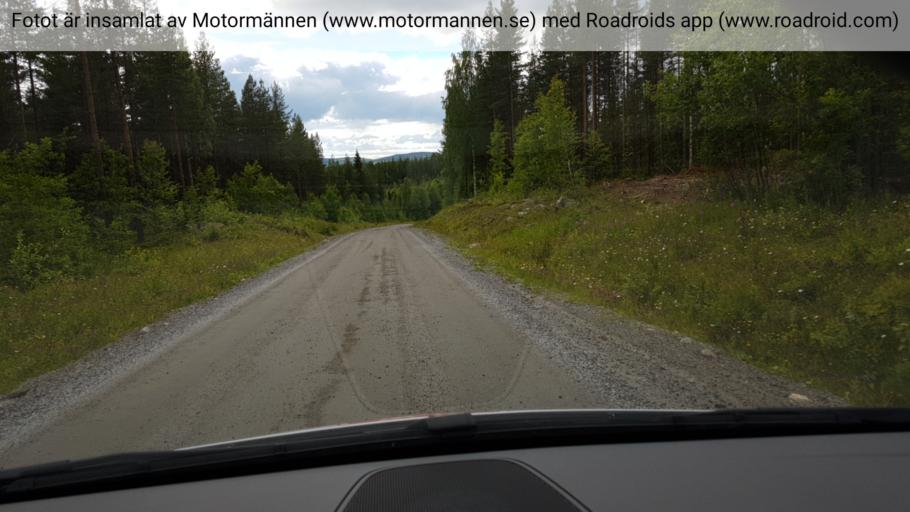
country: SE
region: Vaesterbotten
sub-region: Dorotea Kommun
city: Dorotea
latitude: 63.9310
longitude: 16.1497
